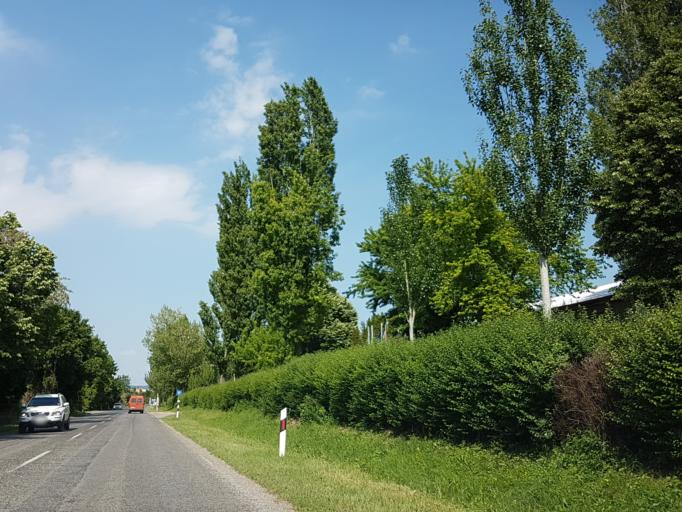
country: HU
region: Veszprem
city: Balatonfured
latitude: 46.9404
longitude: 17.8653
